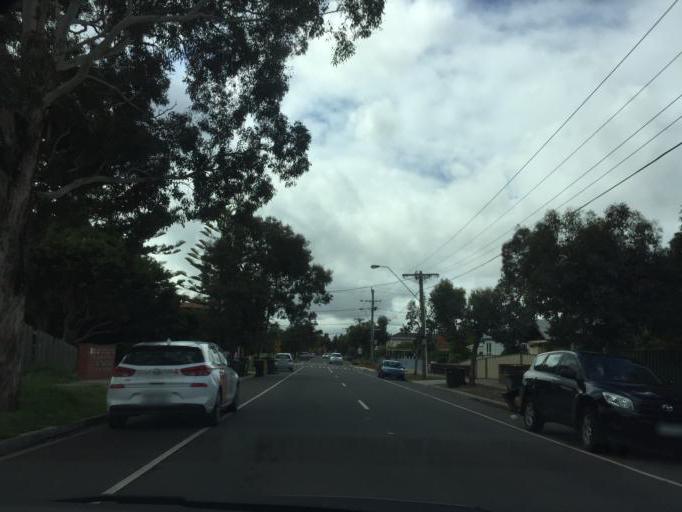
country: AU
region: Victoria
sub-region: Brimbank
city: Sunshine West
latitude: -37.7837
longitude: 144.8236
